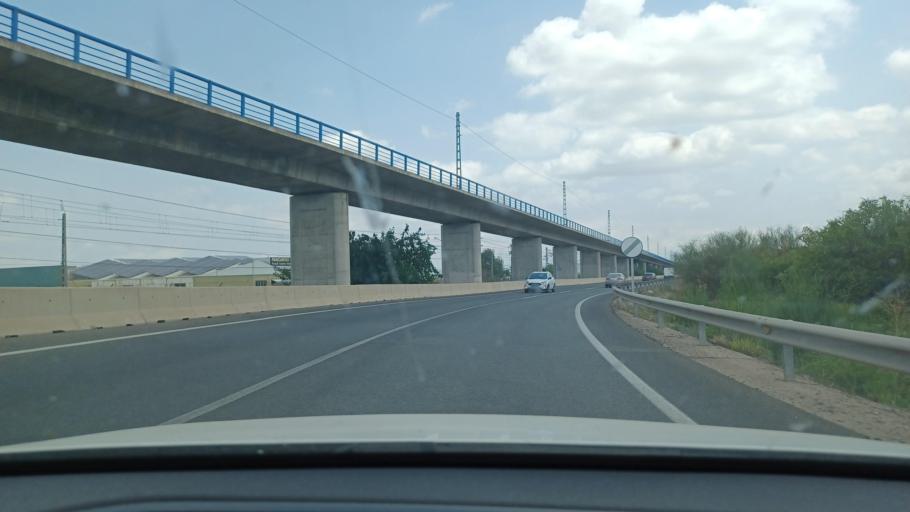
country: ES
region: Valencia
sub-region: Provincia de Valencia
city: Valles
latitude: 38.9797
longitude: -0.5530
